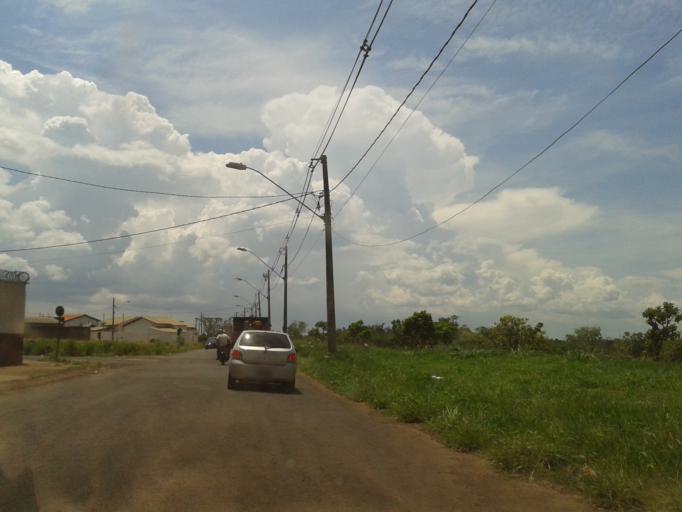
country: BR
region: Minas Gerais
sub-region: Araguari
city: Araguari
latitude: -18.6756
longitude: -48.1932
